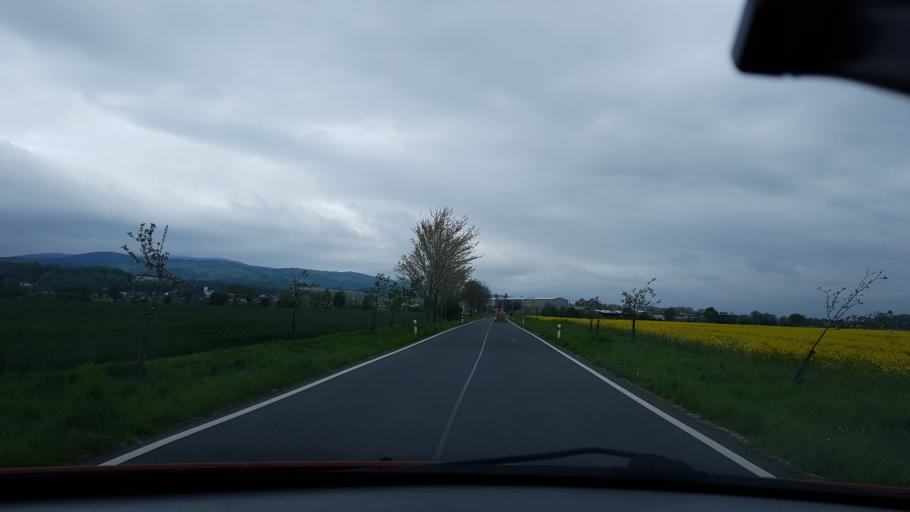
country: CZ
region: Olomoucky
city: Javornik
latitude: 50.3897
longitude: 17.0297
